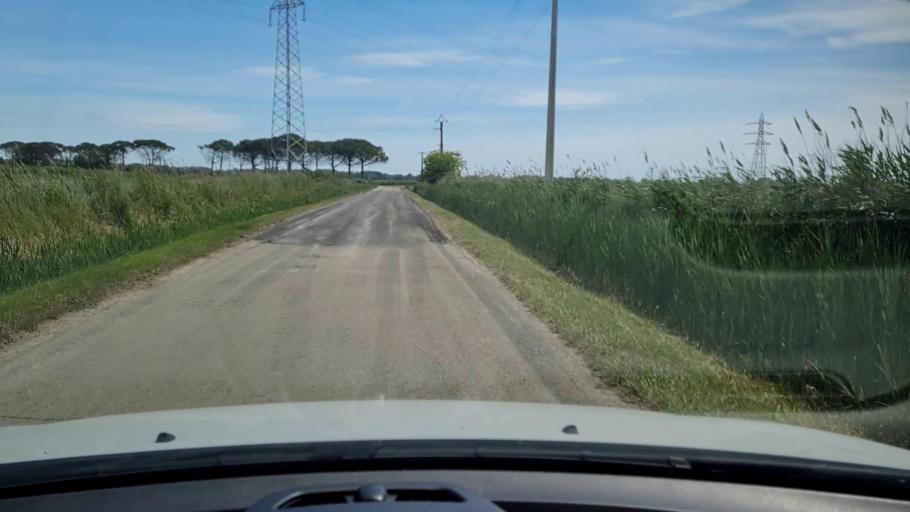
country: FR
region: Languedoc-Roussillon
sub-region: Departement du Gard
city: Saint-Gilles
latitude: 43.5751
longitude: 4.3967
